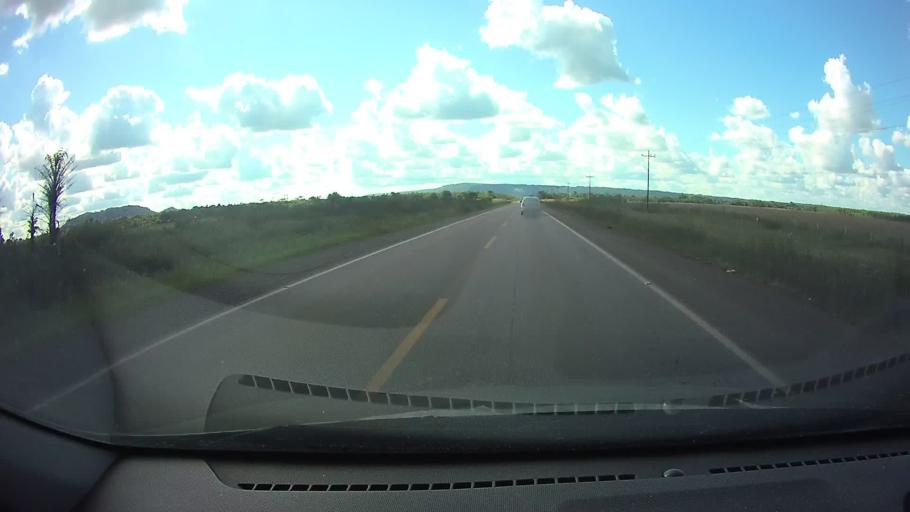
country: PY
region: Paraguari
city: Sapucai
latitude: -25.7238
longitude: -56.8278
